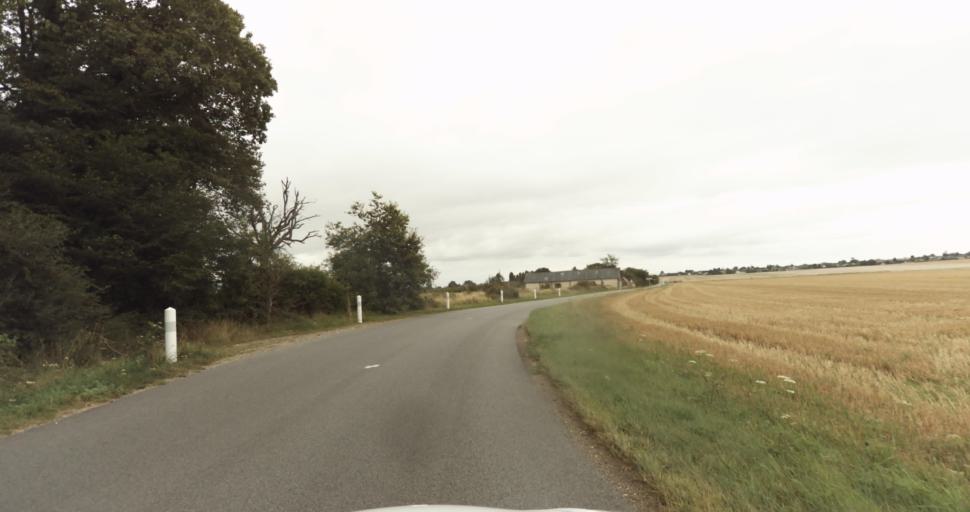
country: FR
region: Haute-Normandie
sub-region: Departement de l'Eure
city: Arnieres-sur-Iton
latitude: 48.9642
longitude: 1.1152
